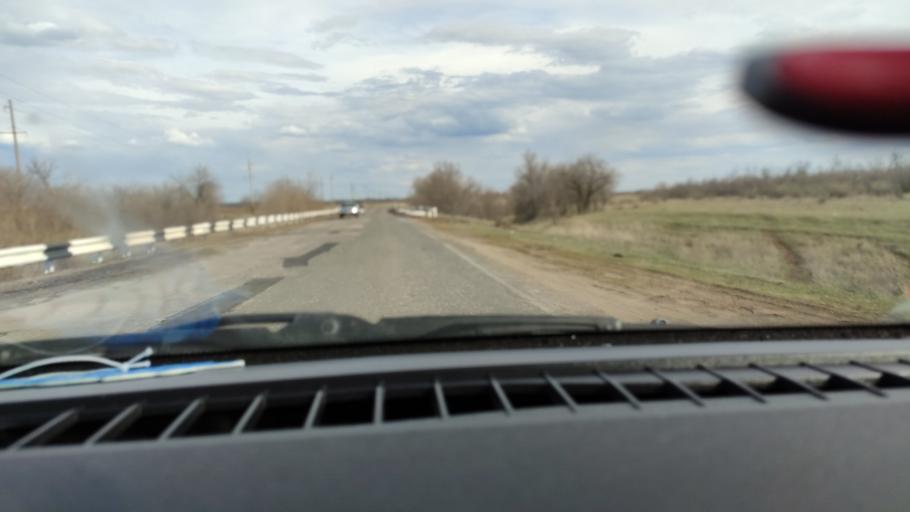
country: RU
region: Saratov
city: Rovnoye
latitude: 51.0555
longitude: 46.0326
